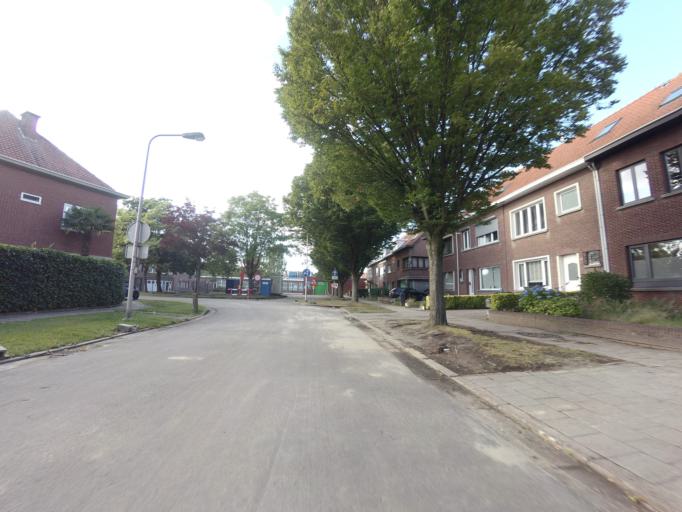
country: BE
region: Flanders
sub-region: Provincie Antwerpen
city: Edegem
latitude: 51.1608
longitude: 4.4233
